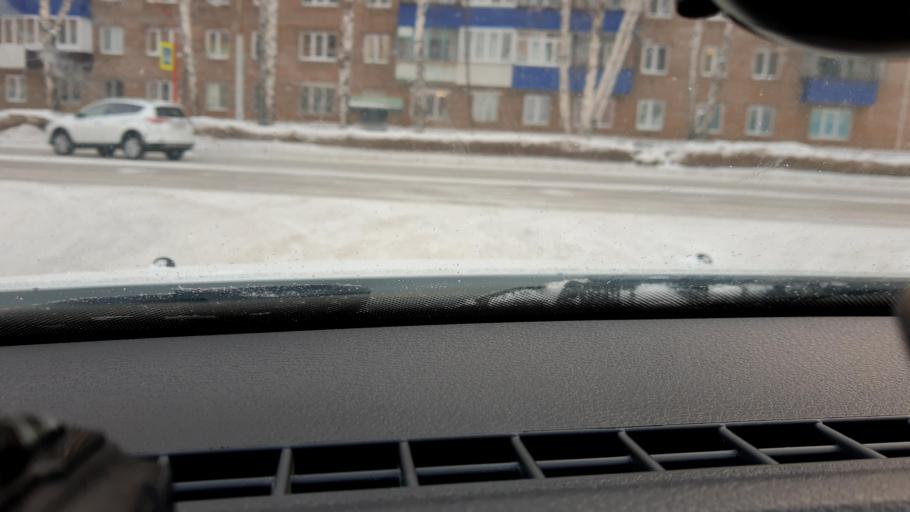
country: RU
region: Bashkortostan
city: Sterlitamak
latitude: 53.6352
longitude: 55.9016
